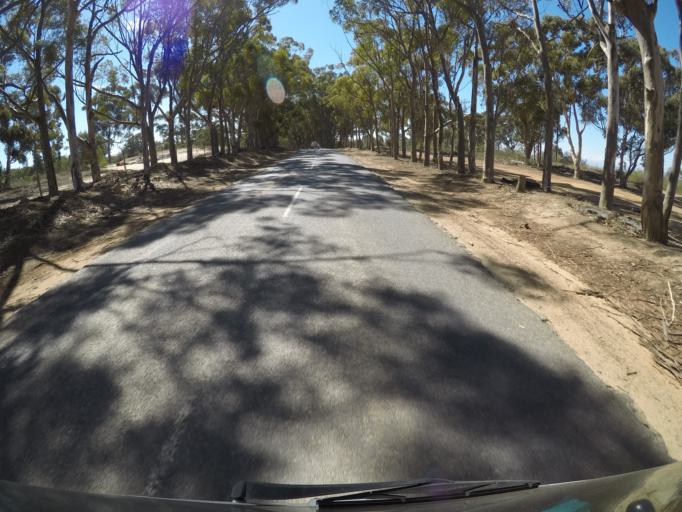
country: ZA
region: Western Cape
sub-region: City of Cape Town
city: Sunset Beach
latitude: -33.7592
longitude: 18.5537
